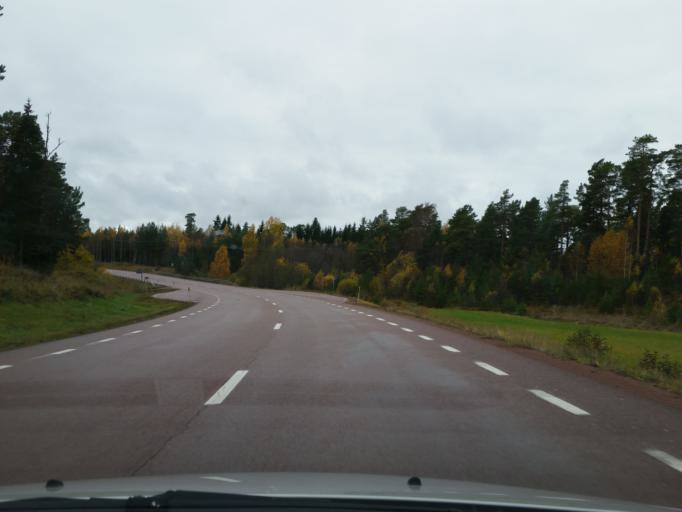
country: AX
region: Alands landsbygd
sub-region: Lumparland
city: Lumparland
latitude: 60.0849
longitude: 20.2397
